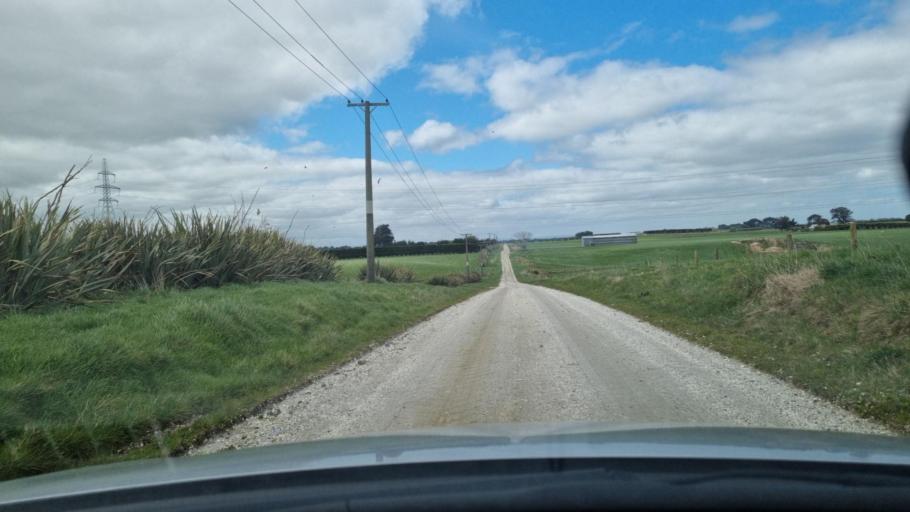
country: NZ
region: Southland
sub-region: Invercargill City
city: Invercargill
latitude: -46.4431
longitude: 168.4493
